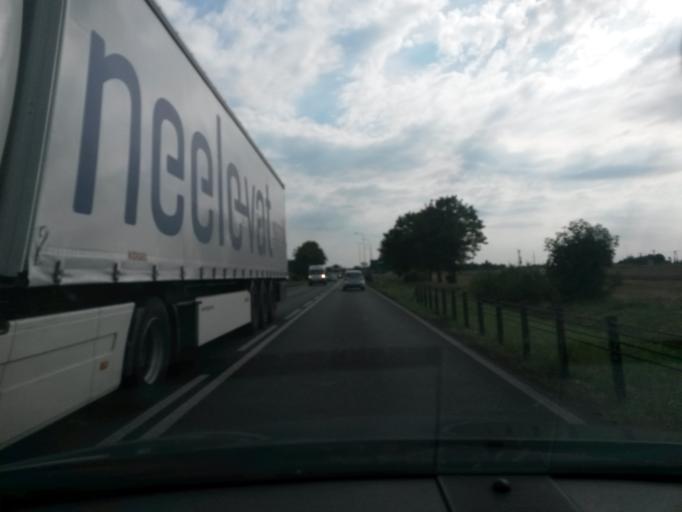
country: PL
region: Greater Poland Voivodeship
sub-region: Powiat rawicki
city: Rawicz
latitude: 51.6297
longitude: 16.8978
